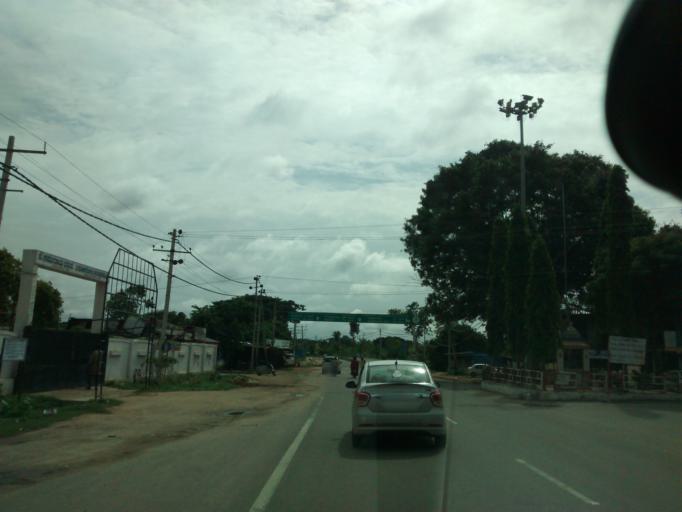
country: IN
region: Karnataka
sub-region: Tumkur
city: Koratagere
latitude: 13.5138
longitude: 77.2272
